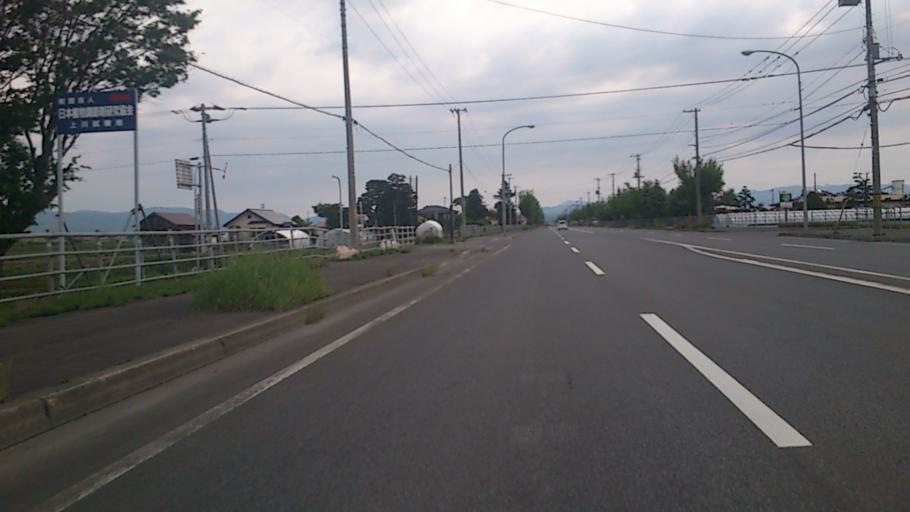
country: JP
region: Hokkaido
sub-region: Asahikawa-shi
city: Asahikawa
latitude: 43.8270
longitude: 142.4604
